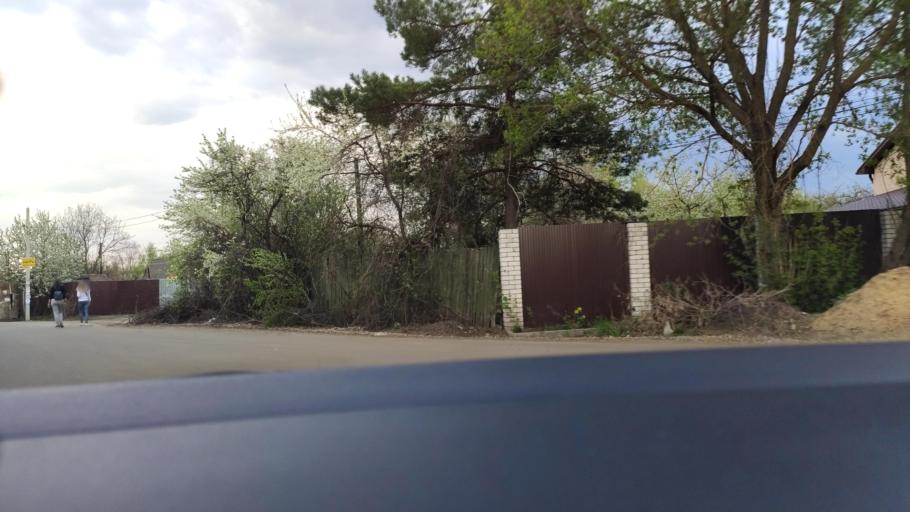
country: RU
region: Voronezj
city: Voronezh
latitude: 51.6078
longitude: 39.1518
